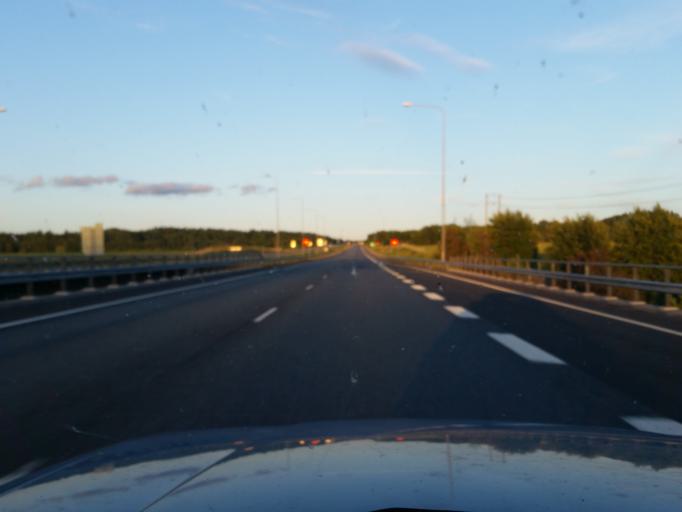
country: FI
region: Varsinais-Suomi
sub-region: Salo
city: Salo
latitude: 60.4151
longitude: 23.1775
